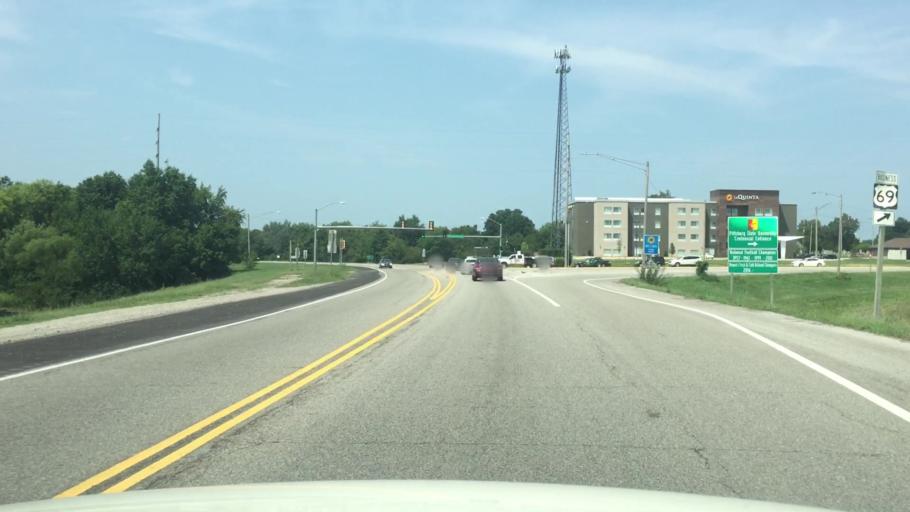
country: US
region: Kansas
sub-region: Crawford County
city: Pittsburg
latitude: 37.3805
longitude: -94.7072
